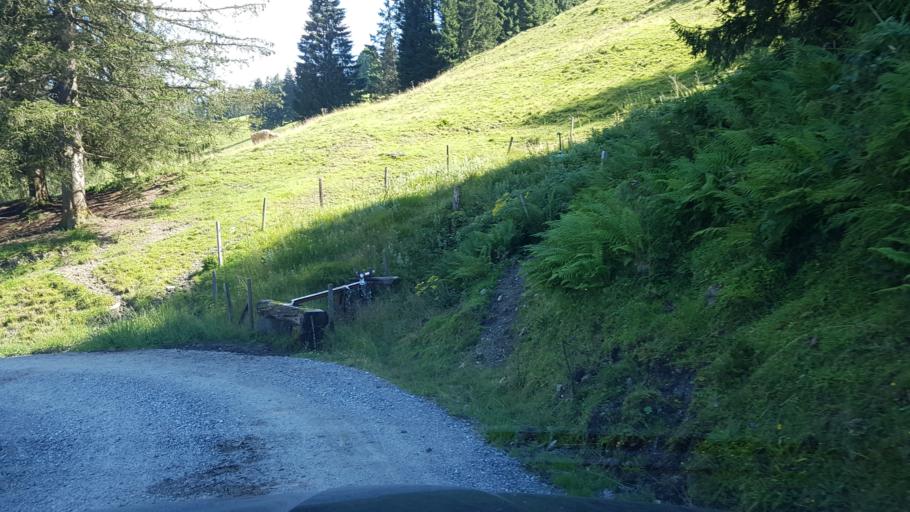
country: AT
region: Salzburg
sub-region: Politischer Bezirk Sankt Johann im Pongau
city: Dorfgastein
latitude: 47.2522
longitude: 13.0759
